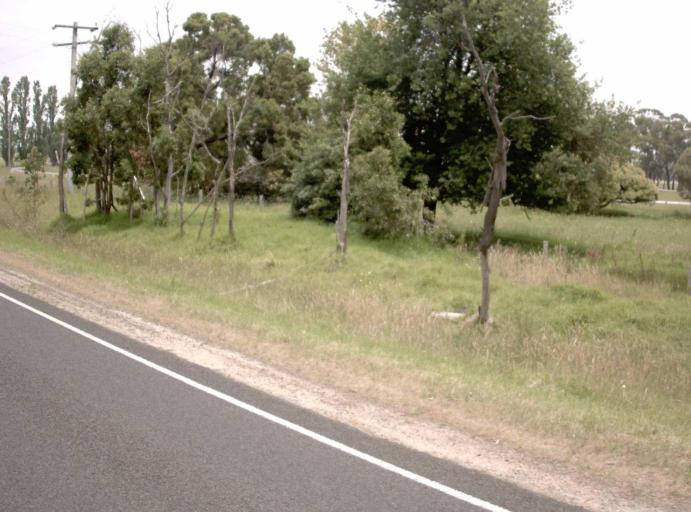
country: AU
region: Victoria
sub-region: Latrobe
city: Traralgon
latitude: -38.4710
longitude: 146.7174
